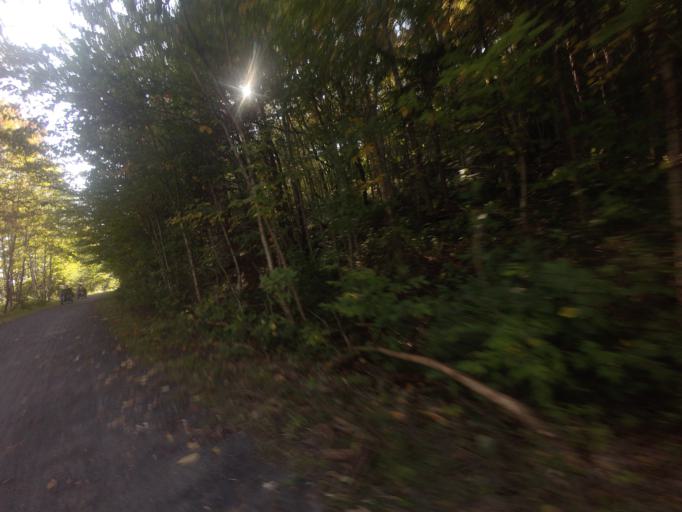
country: CA
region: Quebec
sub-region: Laurentides
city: Sainte-Agathe-des-Monts
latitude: 46.0502
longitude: -74.2728
